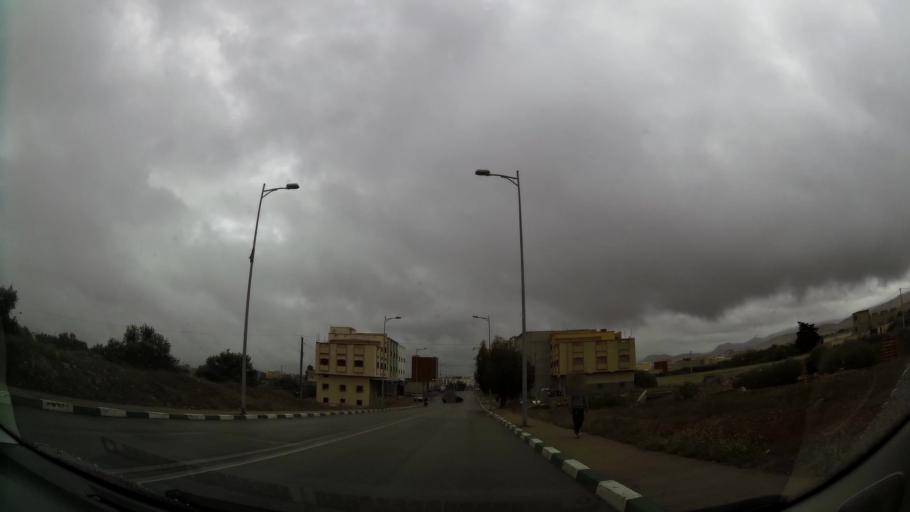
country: MA
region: Oriental
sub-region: Nador
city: Midar
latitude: 35.0507
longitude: -3.4475
